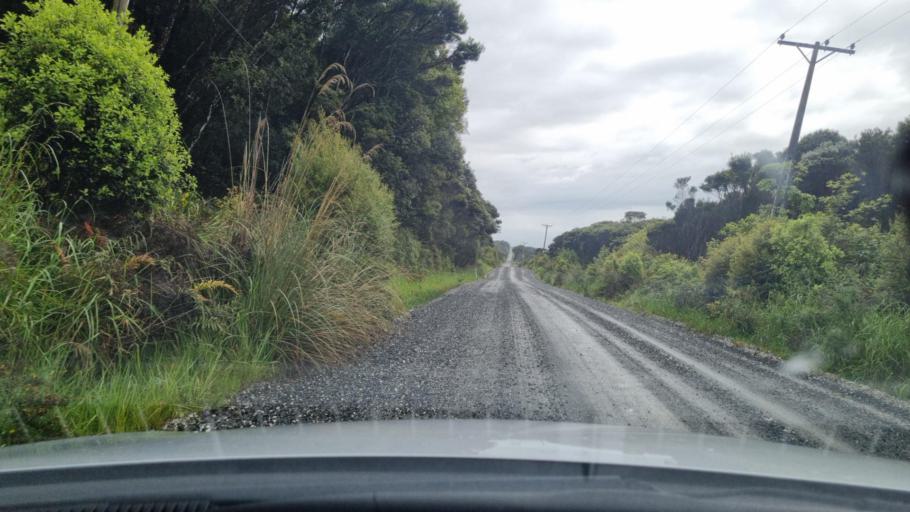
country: NZ
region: Southland
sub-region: Invercargill City
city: Bluff
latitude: -46.5413
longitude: 168.2636
